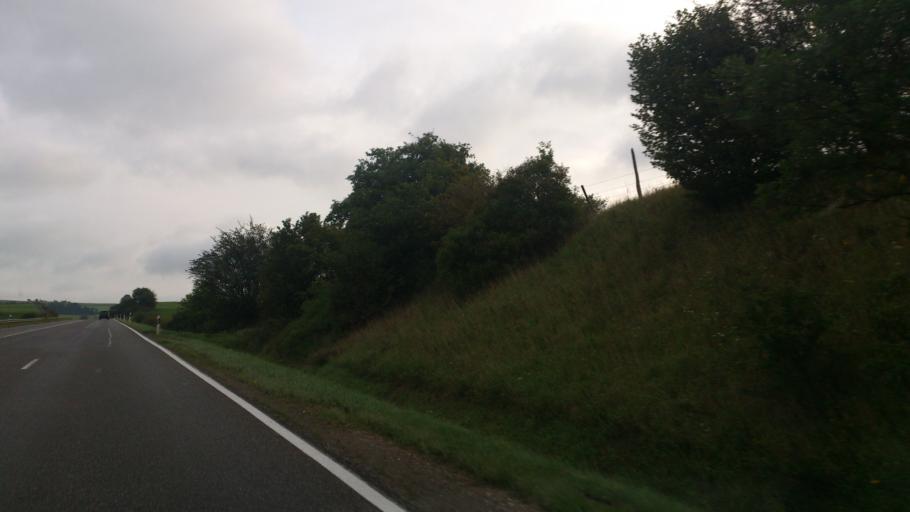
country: DE
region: Rheinland-Pfalz
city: Ohlenhard
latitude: 50.4049
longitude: 6.7353
